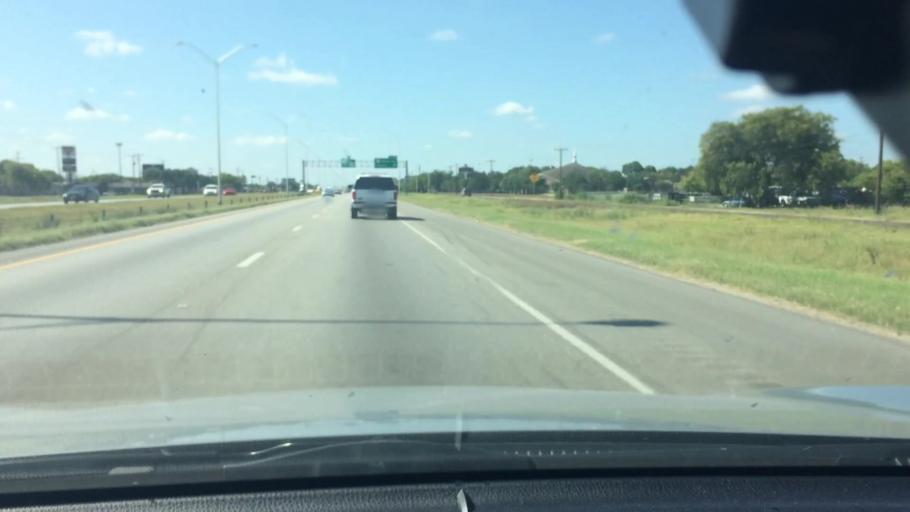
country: US
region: Texas
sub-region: Bexar County
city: China Grove
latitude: 29.4105
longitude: -98.3894
